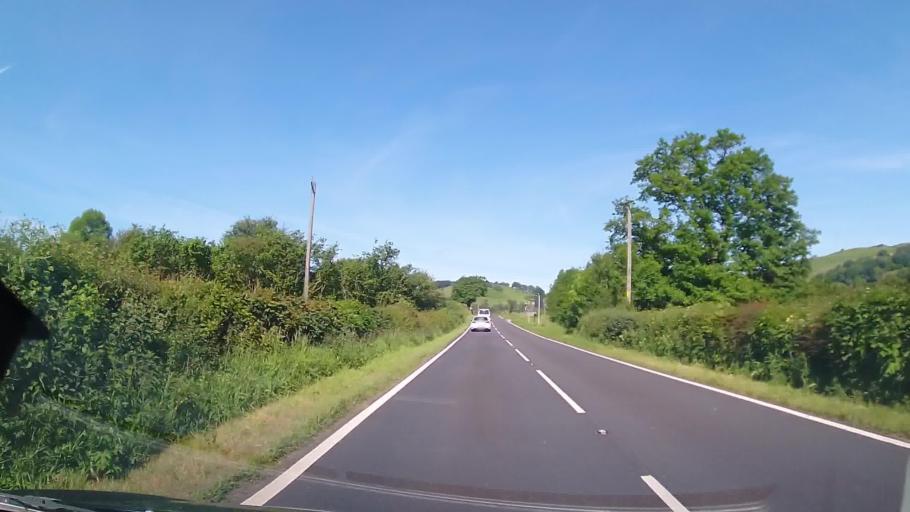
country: GB
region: Wales
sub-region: Sir Powys
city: Llangynog
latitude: 52.6913
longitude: -3.4738
